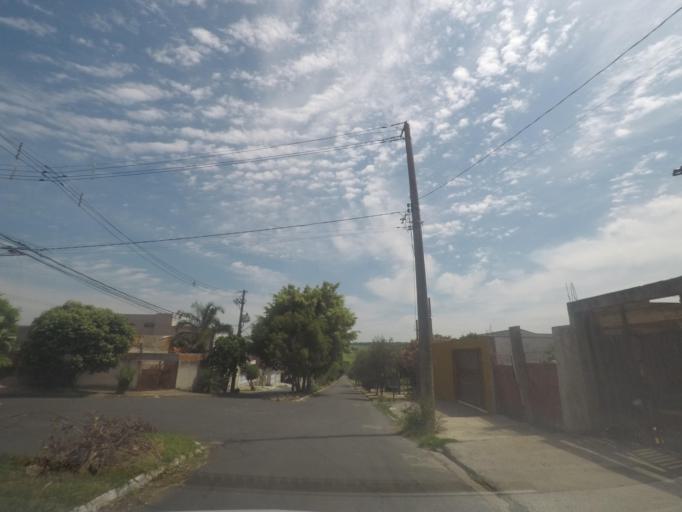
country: BR
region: Sao Paulo
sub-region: Sumare
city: Sumare
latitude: -22.7998
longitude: -47.2666
